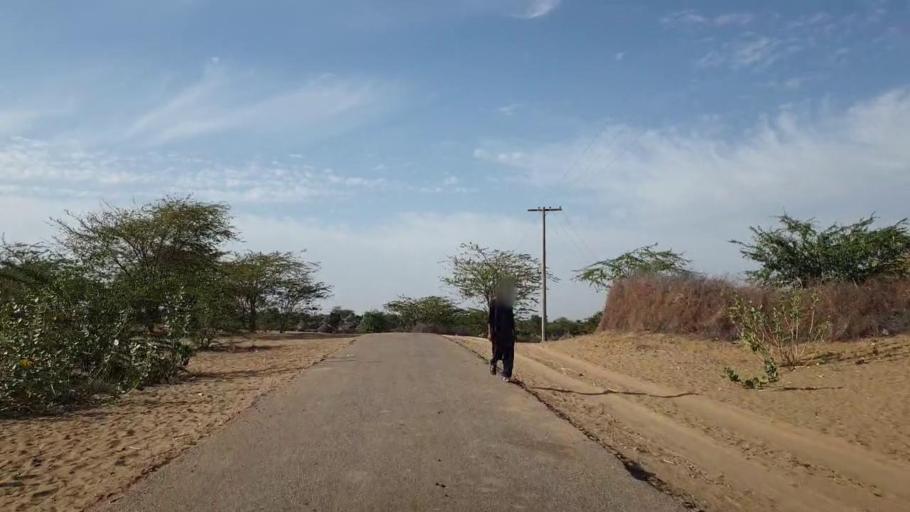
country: PK
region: Sindh
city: Nabisar
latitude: 25.0424
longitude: 70.0165
